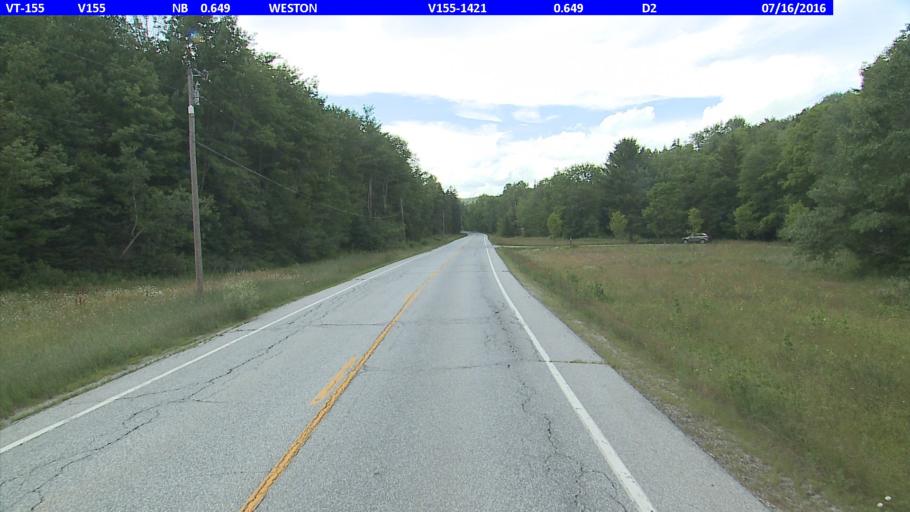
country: US
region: Vermont
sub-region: Windsor County
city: Chester
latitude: 43.3456
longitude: -72.7899
